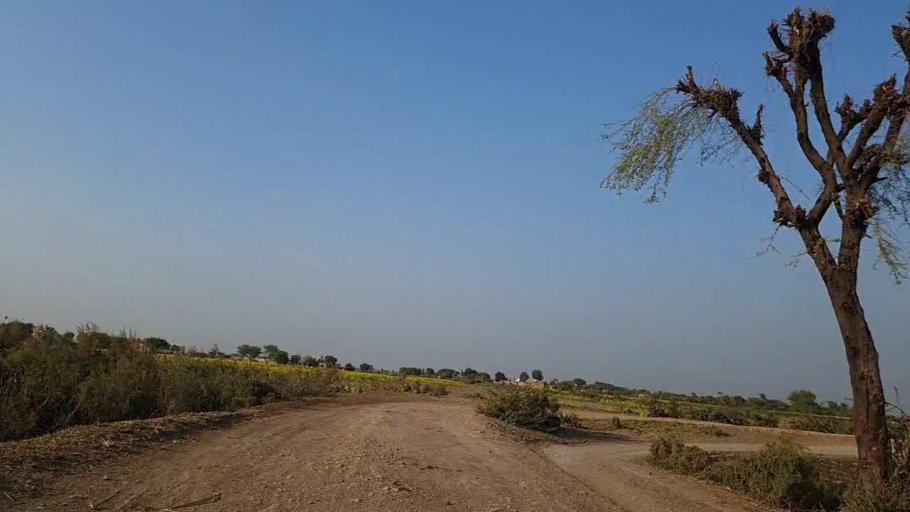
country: PK
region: Sindh
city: Sakrand
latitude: 26.1095
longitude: 68.3685
